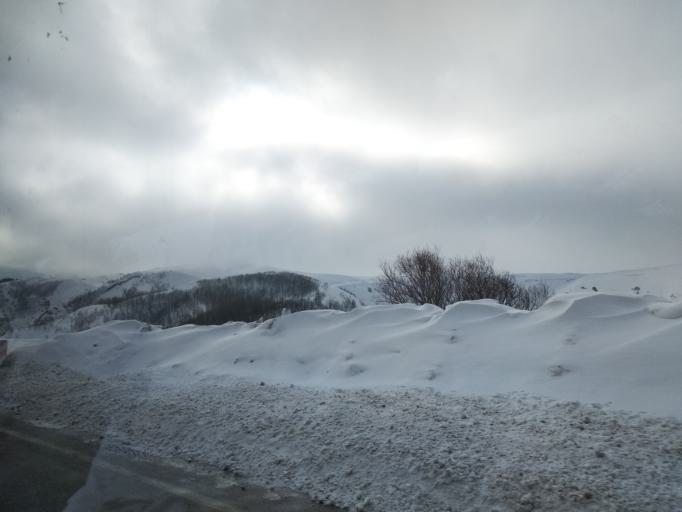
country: TR
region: Erzincan
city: Catalarmut
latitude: 39.8935
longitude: 39.3747
